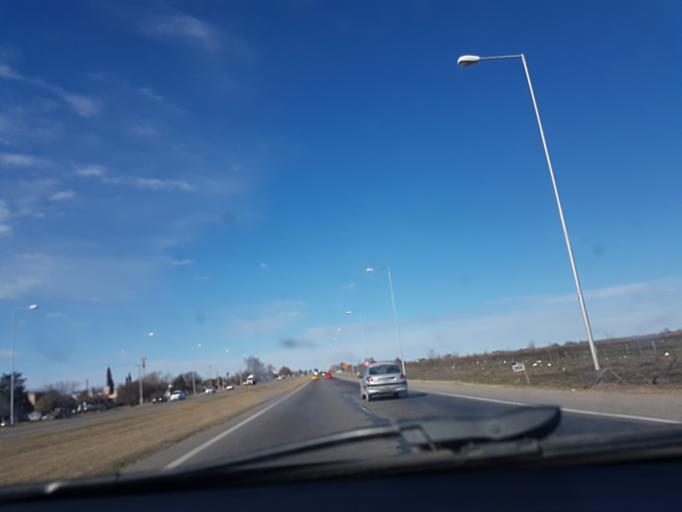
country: AR
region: Cordoba
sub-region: Departamento de Capital
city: Cordoba
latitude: -31.4049
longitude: -64.2697
